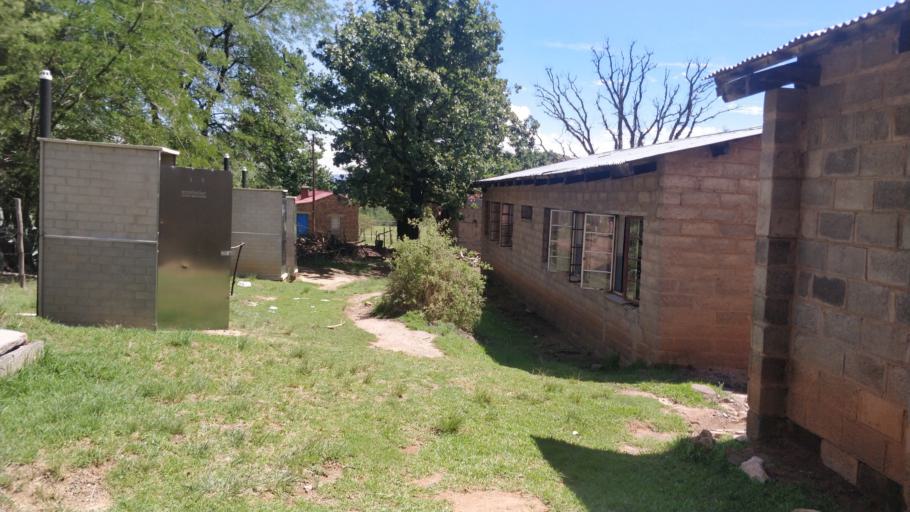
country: LS
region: Maseru
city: Nako
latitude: -29.6295
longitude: 27.5054
